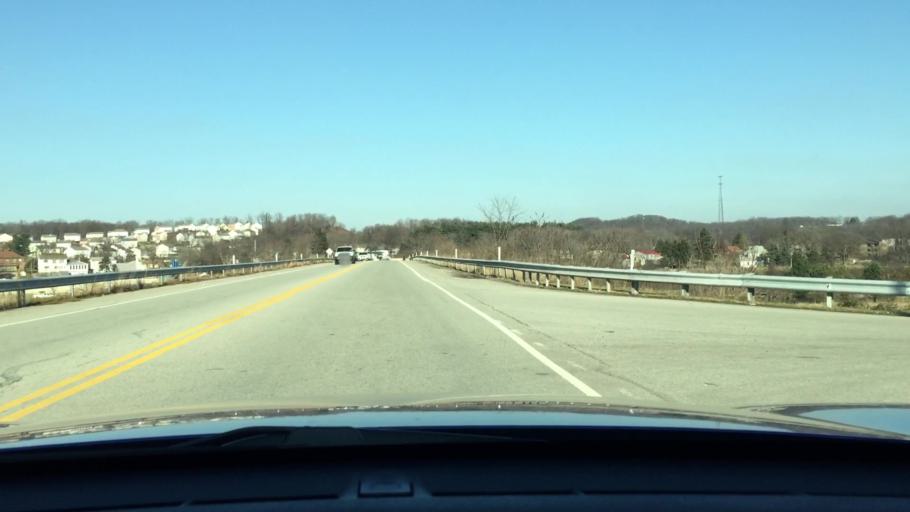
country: US
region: Pennsylvania
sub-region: Westmoreland County
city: New Stanton
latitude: 40.2240
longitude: -79.6110
